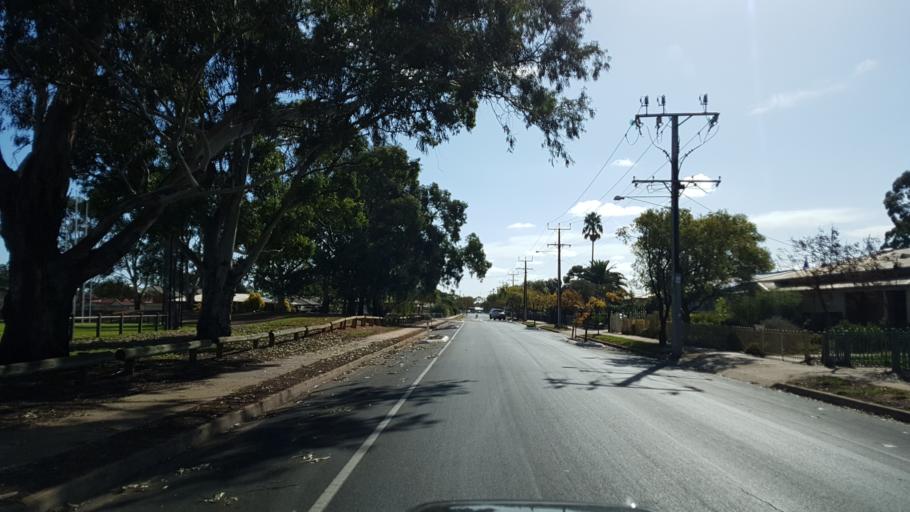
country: AU
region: South Australia
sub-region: Salisbury
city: Salisbury
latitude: -34.7516
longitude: 138.6335
